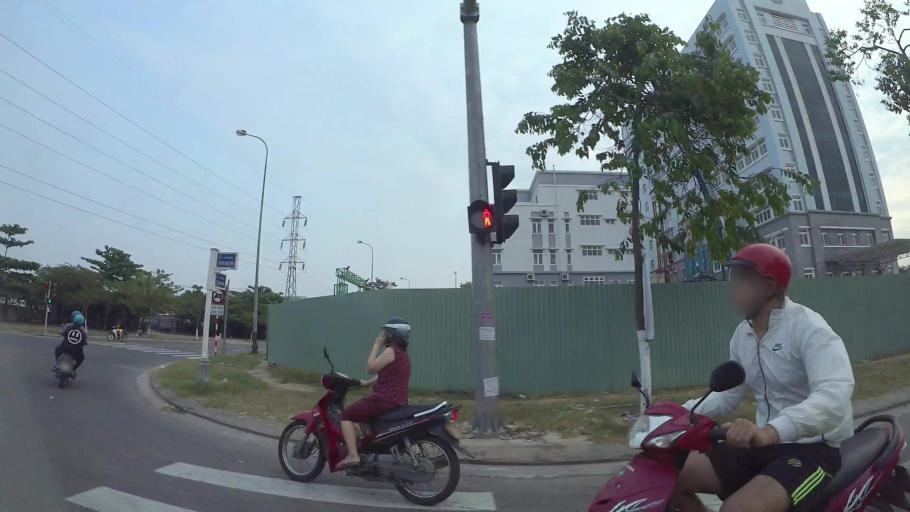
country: VN
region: Da Nang
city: Cam Le
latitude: 16.0323
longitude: 108.2186
